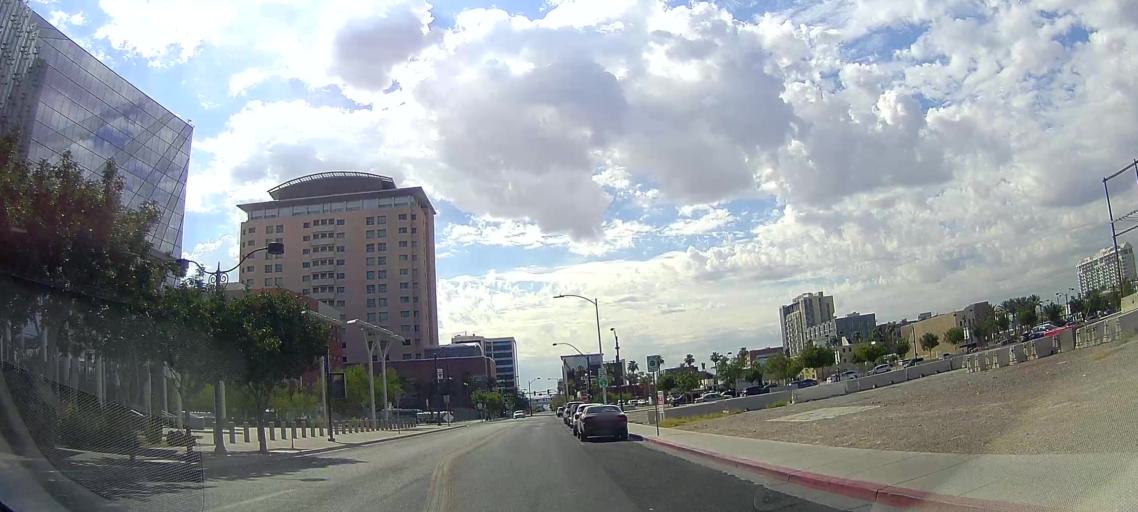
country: US
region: Nevada
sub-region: Clark County
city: Las Vegas
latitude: 36.1670
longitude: -115.1491
